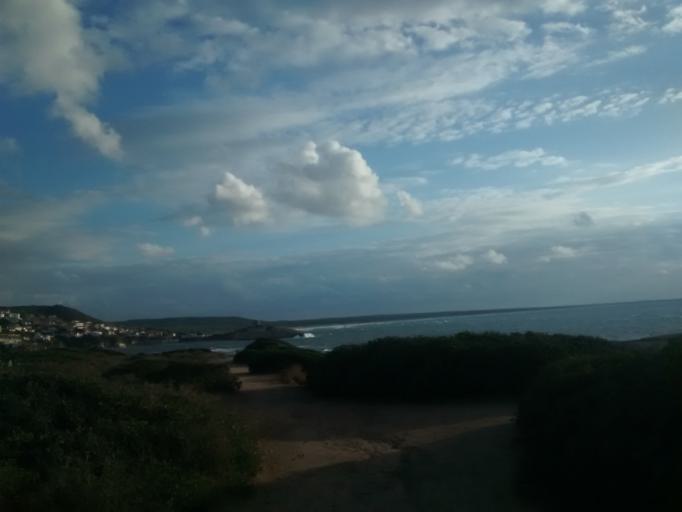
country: IT
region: Sardinia
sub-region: Provincia di Oristano
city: Narbolia
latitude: 40.0952
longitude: 8.4896
